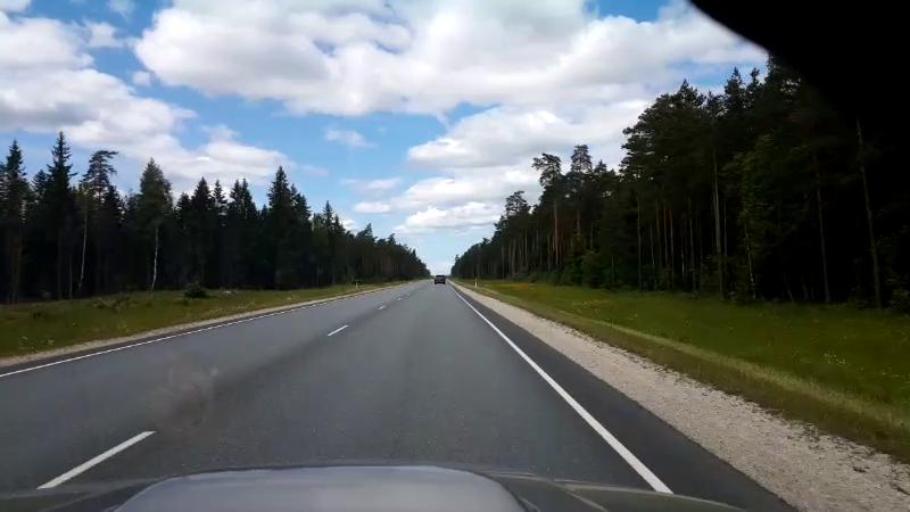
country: EE
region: Raplamaa
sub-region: Maerjamaa vald
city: Marjamaa
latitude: 59.0121
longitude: 24.4555
